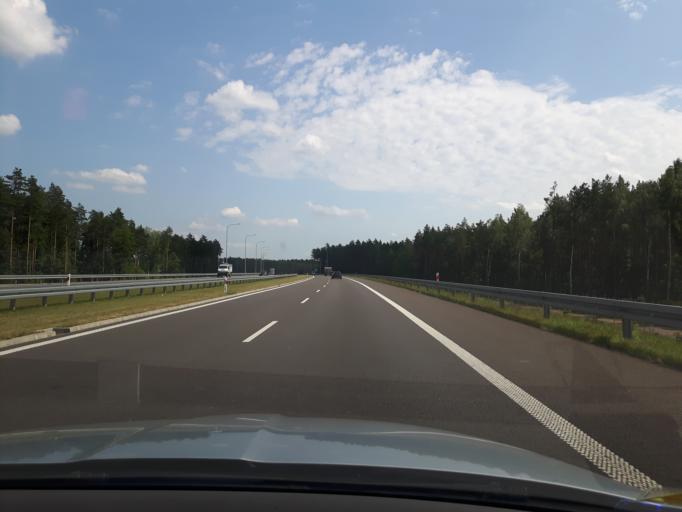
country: PL
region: Warmian-Masurian Voivodeship
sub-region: Powiat ostrodzki
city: Gierzwald
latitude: 53.5831
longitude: 20.1683
